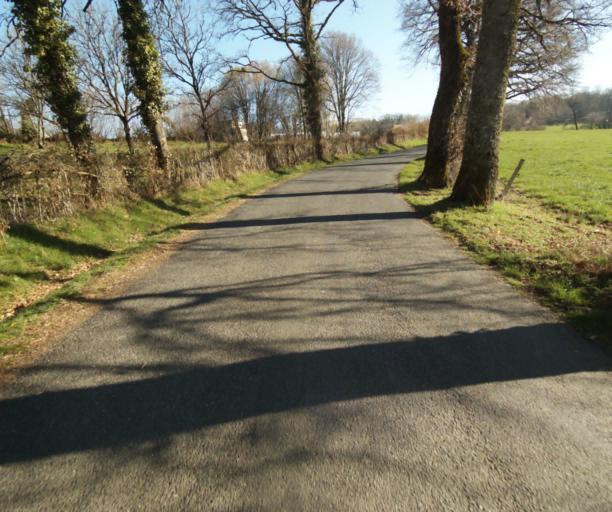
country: FR
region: Limousin
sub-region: Departement de la Correze
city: Saint-Clement
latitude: 45.3829
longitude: 1.6424
